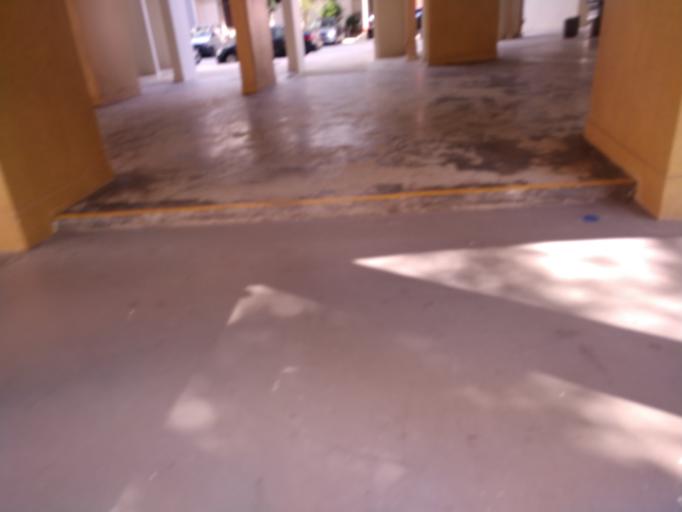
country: SG
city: Singapore
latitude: 1.2872
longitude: 103.8125
